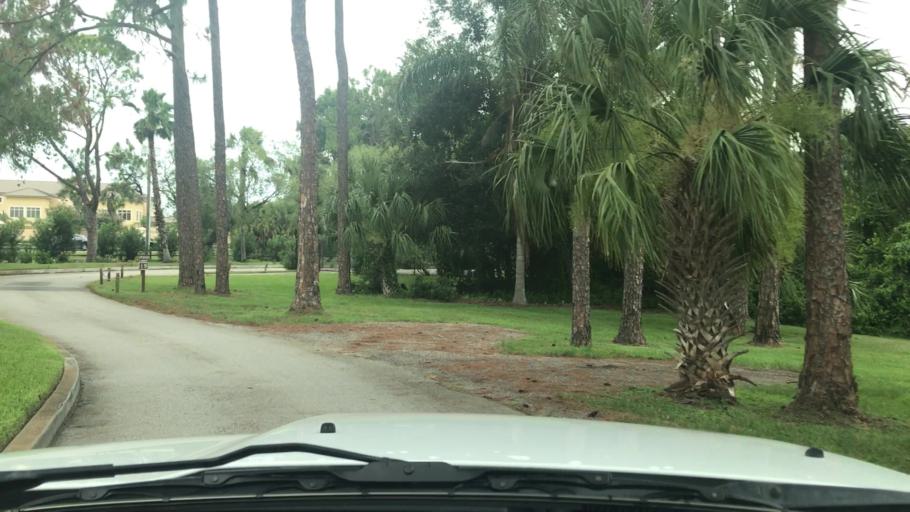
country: US
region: Florida
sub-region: Polk County
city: Cypress Gardens
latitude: 28.0119
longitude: -81.6788
